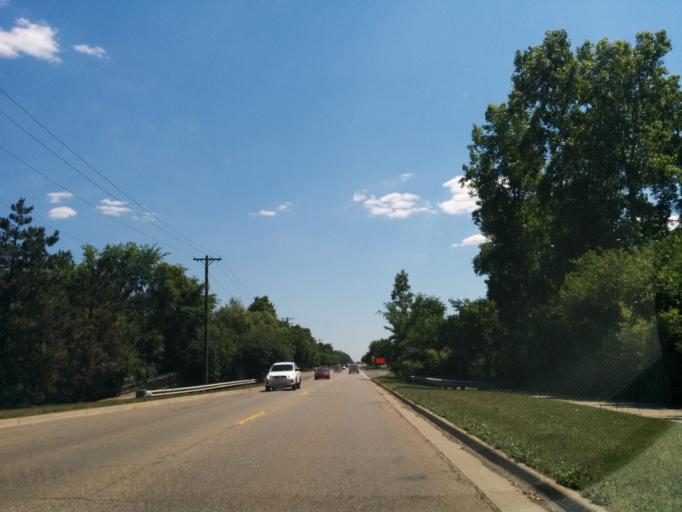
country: US
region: Michigan
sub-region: Oakland County
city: West Bloomfield Township
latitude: 42.5342
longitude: -83.3800
